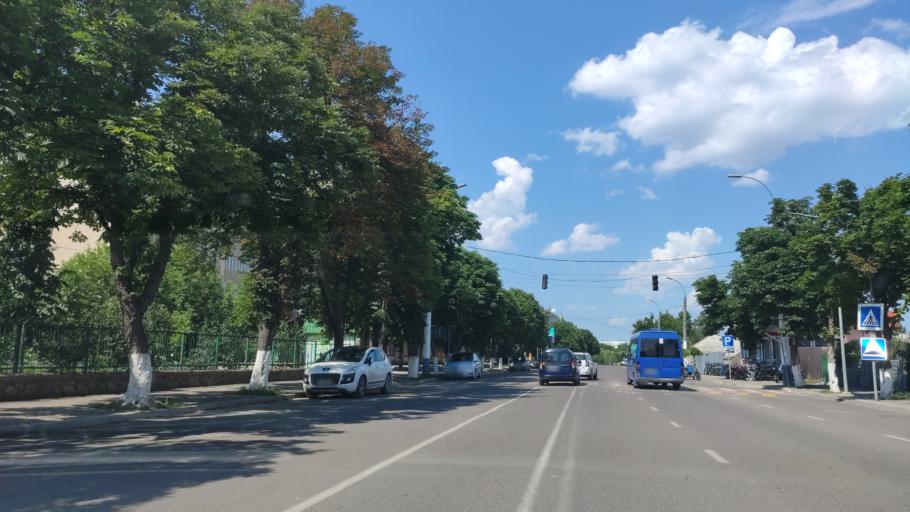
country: MD
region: Raionul Soroca
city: Soroca
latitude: 48.1592
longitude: 28.3027
